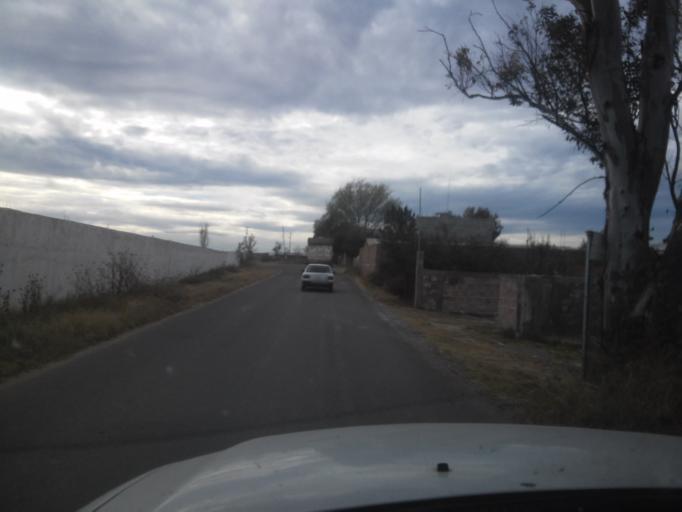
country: MX
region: Durango
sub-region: Durango
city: Jose Refugio Salcido
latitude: 24.0302
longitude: -104.5691
